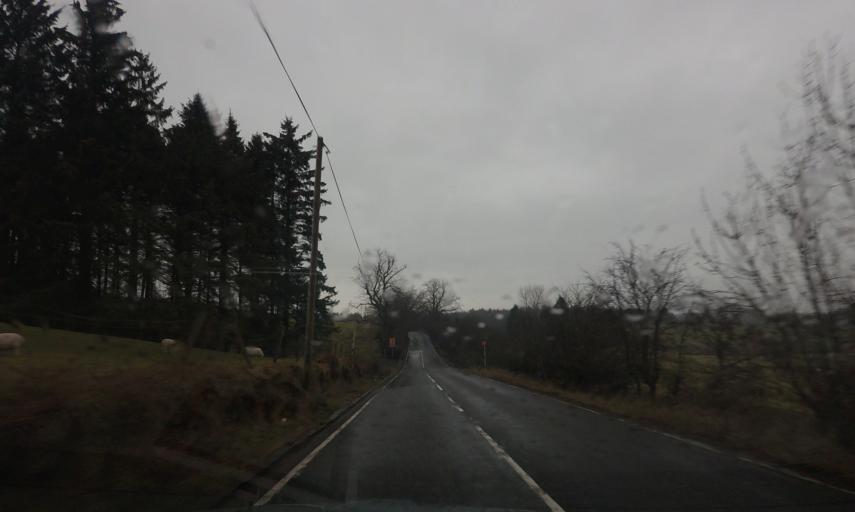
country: GB
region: Scotland
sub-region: East Dunbartonshire
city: Milngavie
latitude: 55.9566
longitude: -4.3592
